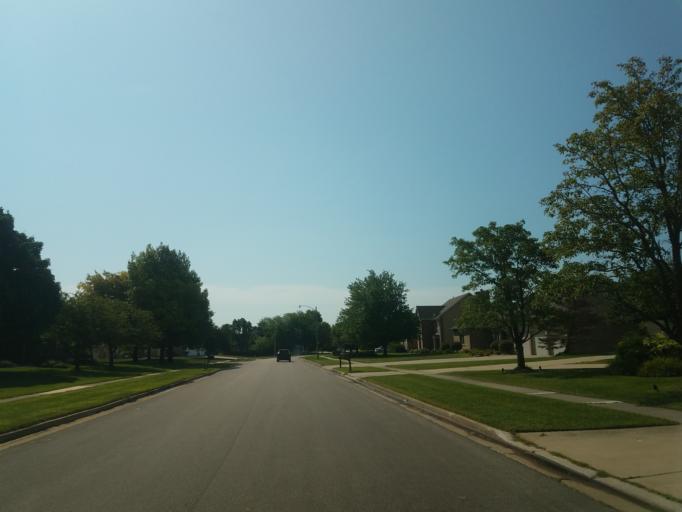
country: US
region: Illinois
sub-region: McLean County
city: Normal
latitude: 40.5050
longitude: -88.9173
